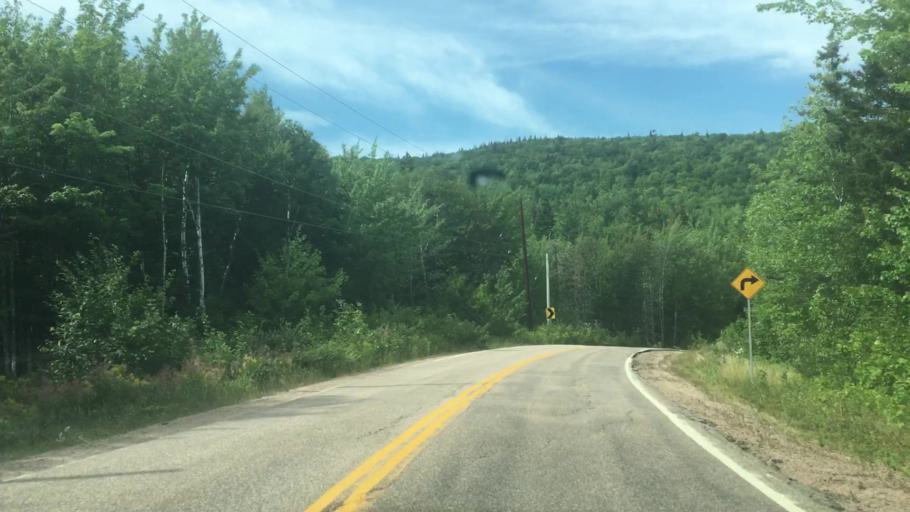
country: CA
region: Nova Scotia
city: Sydney Mines
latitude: 46.6067
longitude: -60.3979
